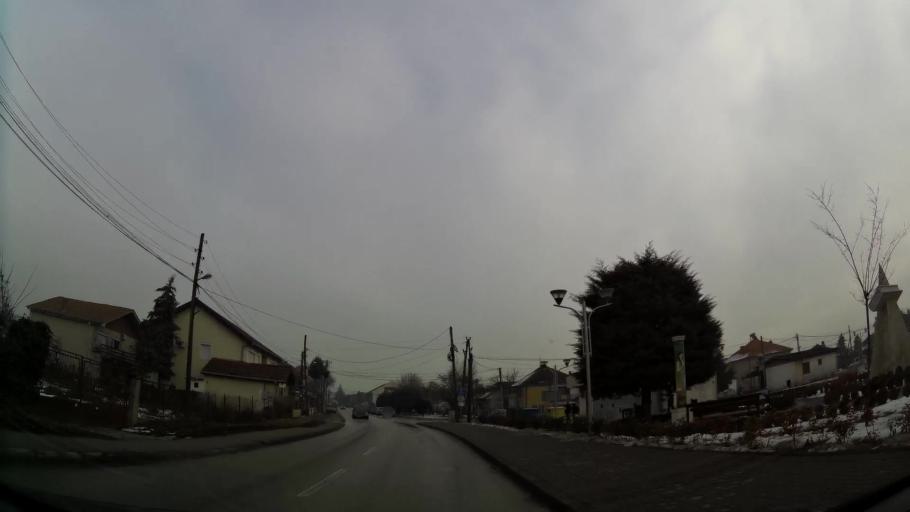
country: MK
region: Ilinden
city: Ilinden
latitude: 41.9947
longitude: 21.5736
